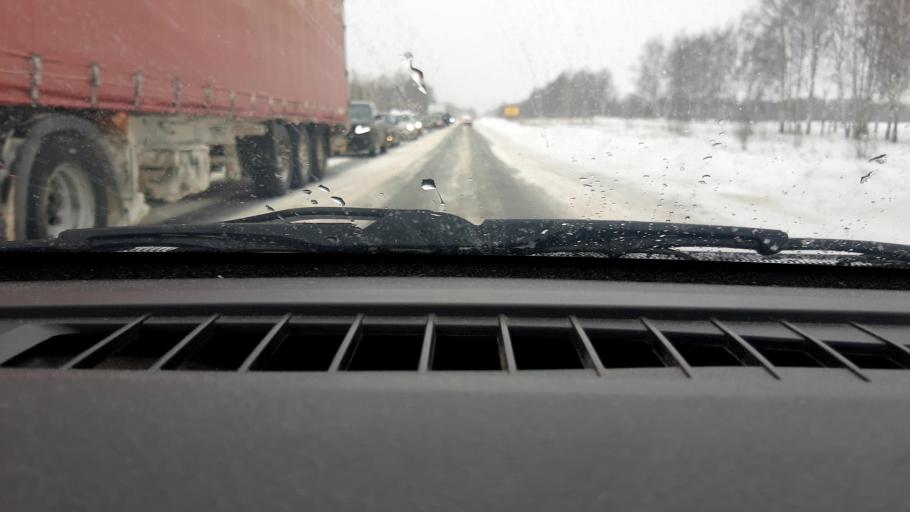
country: RU
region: Vladimir
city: Vorsha
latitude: 56.0635
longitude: 40.1212
